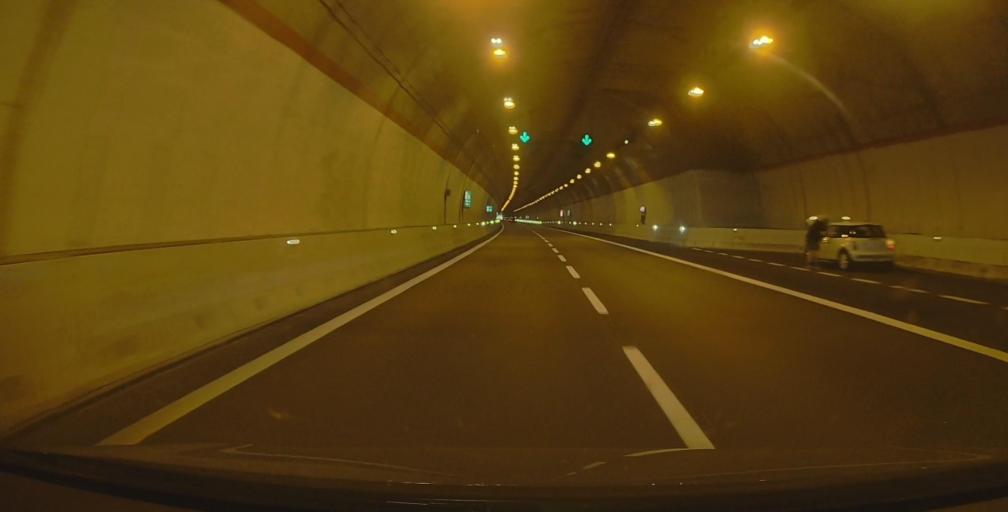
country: IT
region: Campania
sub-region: Provincia di Salerno
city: Casalbuono
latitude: 40.2111
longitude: 15.6747
